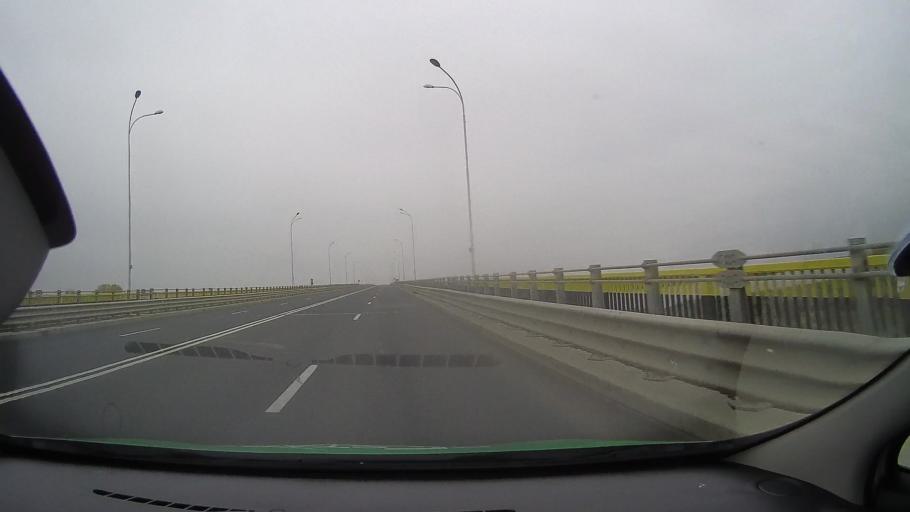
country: RO
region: Ialomita
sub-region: Comuna Giurgeni
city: Giurgeni
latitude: 44.7531
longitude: 27.8841
